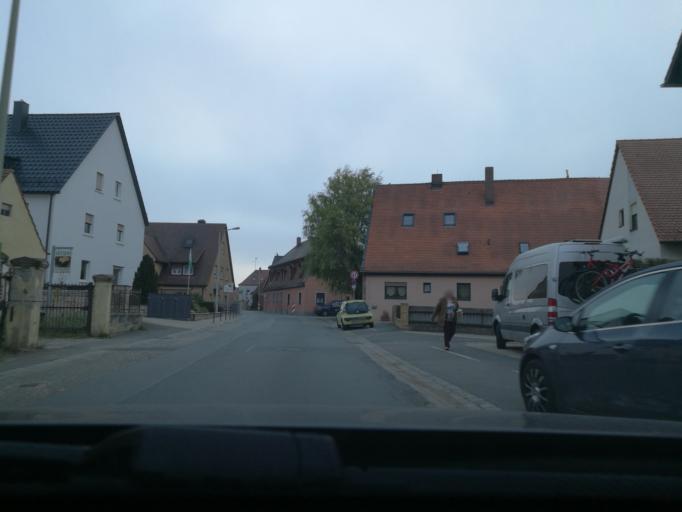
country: DE
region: Bavaria
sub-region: Regierungsbezirk Mittelfranken
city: Wetzendorf
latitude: 49.4891
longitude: 11.0305
